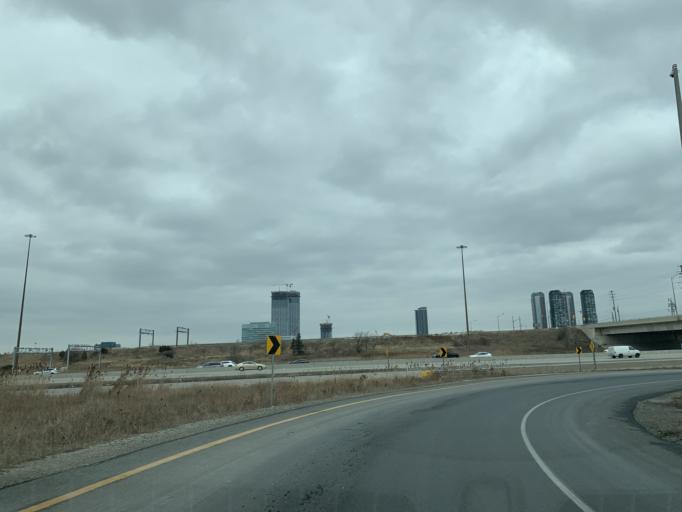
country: CA
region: Ontario
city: Concord
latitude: 43.7849
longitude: -79.5244
